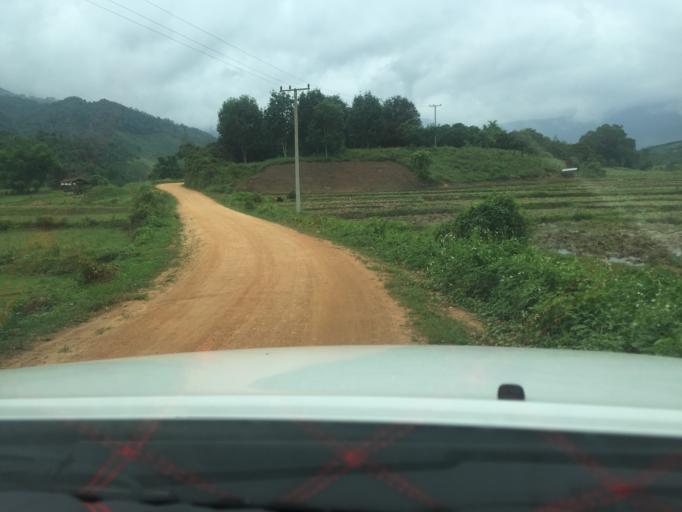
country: TH
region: Phayao
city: Phu Sang
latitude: 19.7364
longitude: 100.4739
